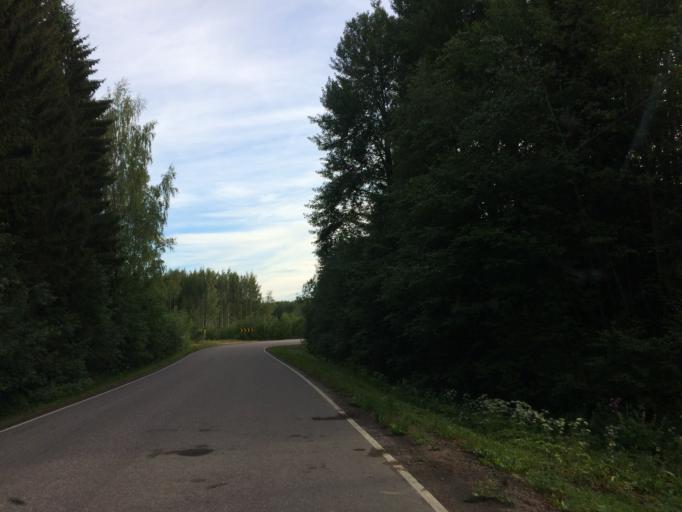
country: FI
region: Haeme
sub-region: Haemeenlinna
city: Janakkala
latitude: 60.8776
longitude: 24.5650
